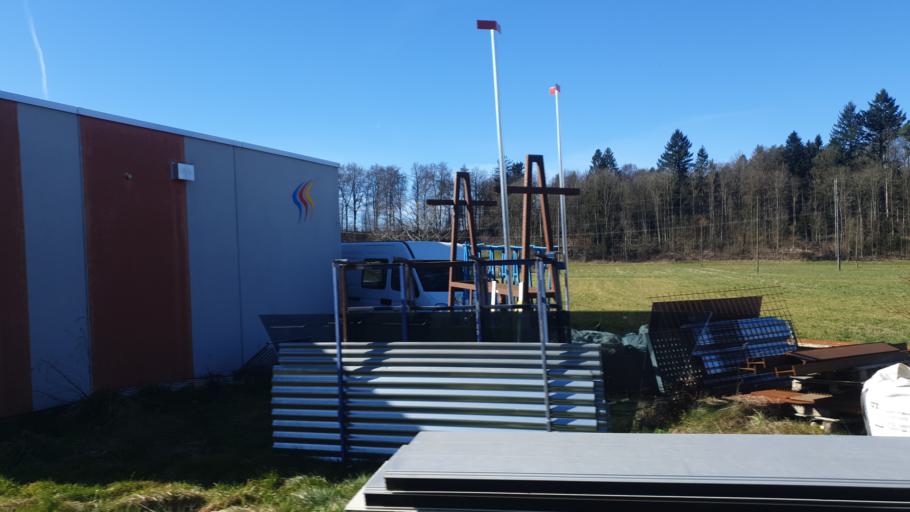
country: CH
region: Bern
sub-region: Oberaargau
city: Lotzwil
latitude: 47.1944
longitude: 7.7859
